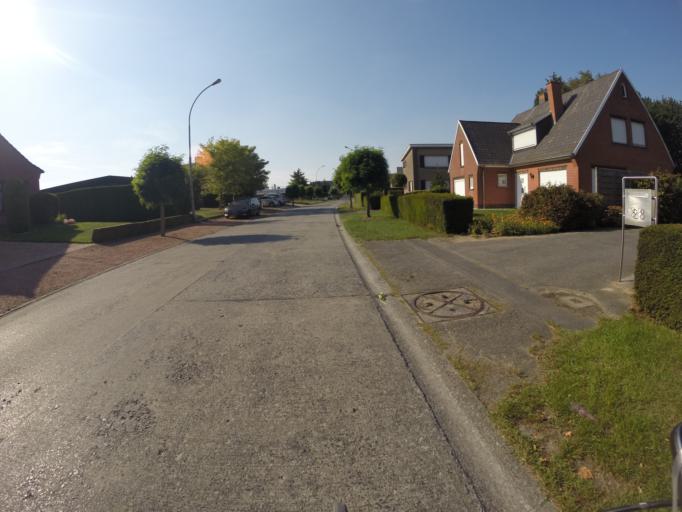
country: BE
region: Flanders
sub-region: Provincie Oost-Vlaanderen
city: Aalter
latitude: 51.0891
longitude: 3.4573
